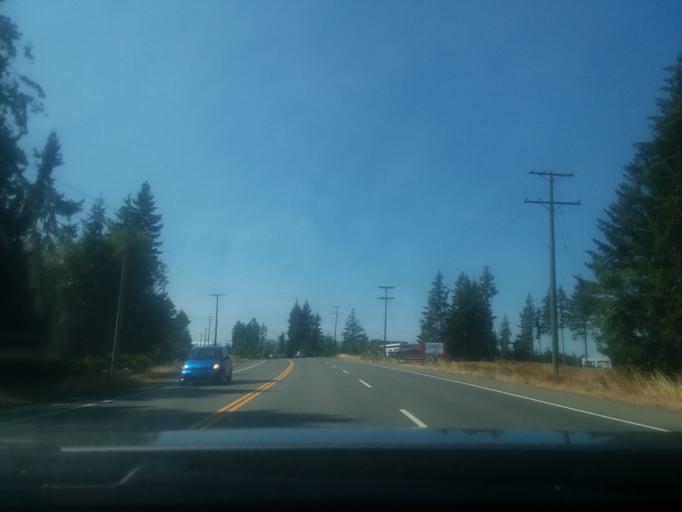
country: CA
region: British Columbia
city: Courtenay
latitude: 49.7149
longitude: -124.9563
